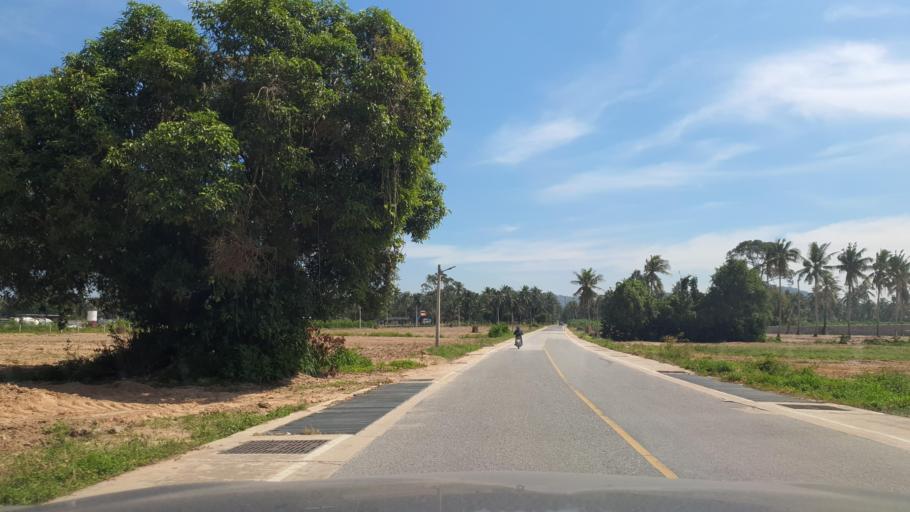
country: TH
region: Chon Buri
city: Bang Lamung
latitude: 12.9845
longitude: 100.9794
